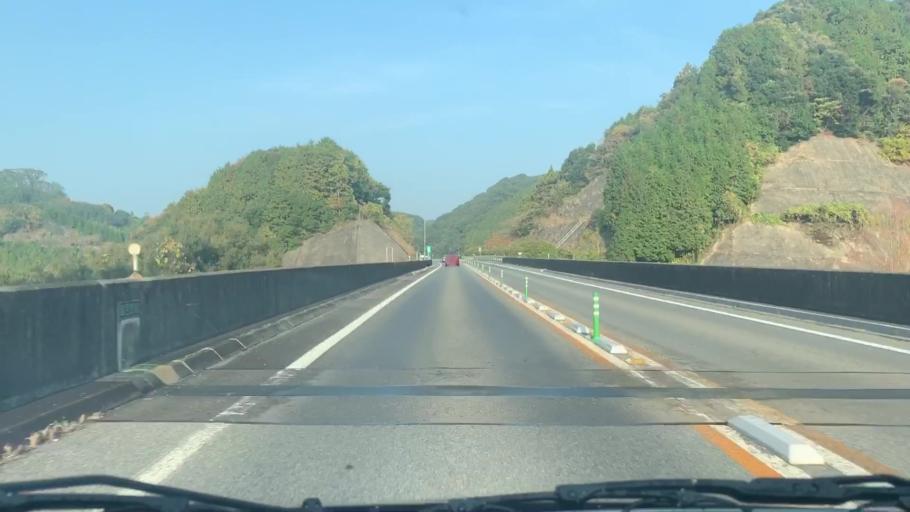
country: JP
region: Saga Prefecture
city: Ureshinomachi-shimojuku
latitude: 33.1452
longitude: 129.9517
